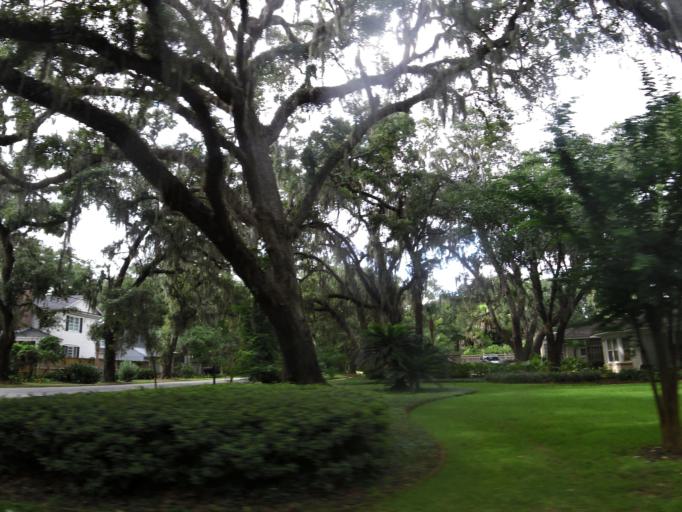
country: US
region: Georgia
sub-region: Glynn County
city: Saint Simons Island
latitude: 31.1391
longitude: -81.3971
